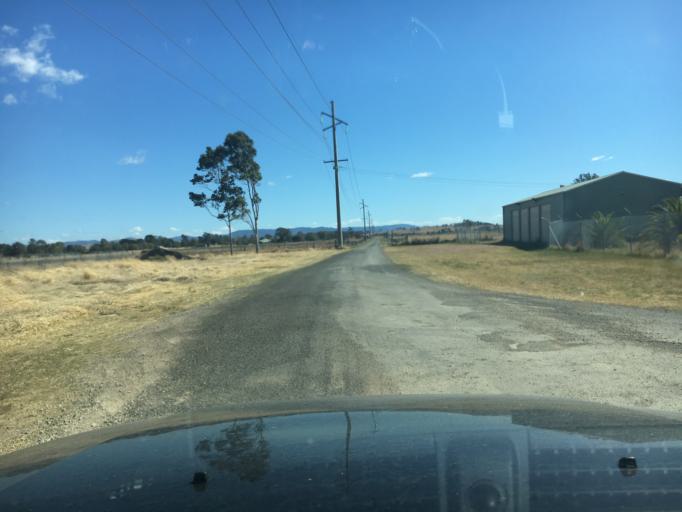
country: AU
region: New South Wales
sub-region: Singleton
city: Singleton
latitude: -32.5908
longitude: 151.1746
